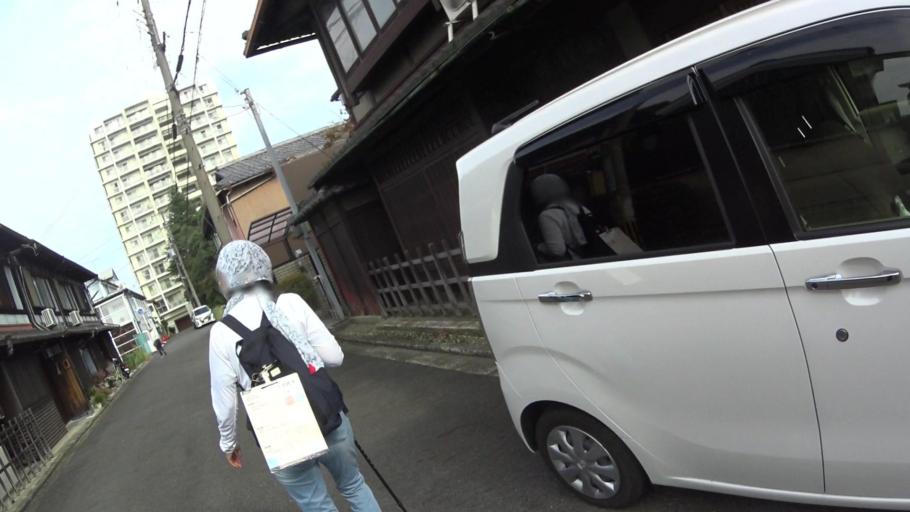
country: JP
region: Osaka
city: Kishiwada
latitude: 34.5039
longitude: 135.3364
